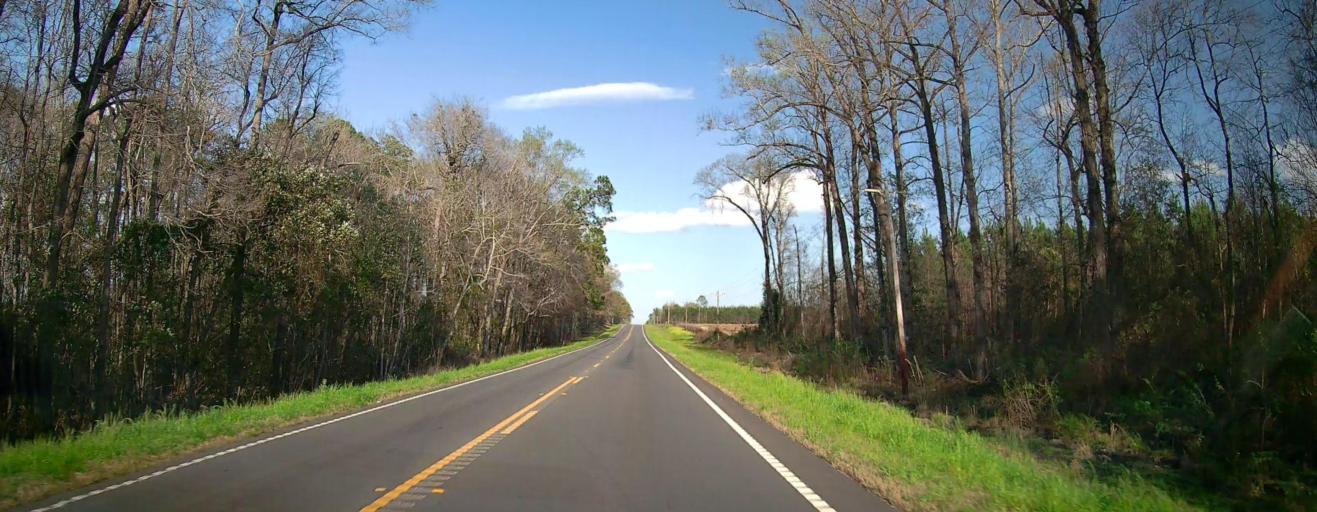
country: US
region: Georgia
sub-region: Toombs County
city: Vidalia
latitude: 32.1993
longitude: -82.4978
